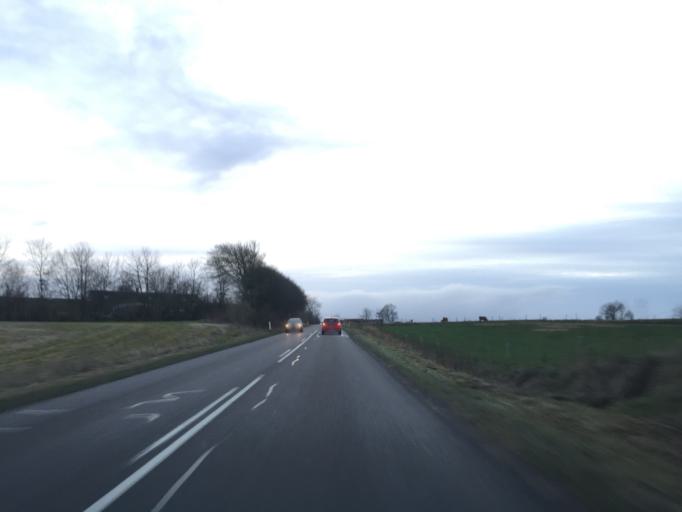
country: DK
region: Central Jutland
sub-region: Viborg Kommune
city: Bjerringbro
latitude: 56.3451
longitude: 9.6522
